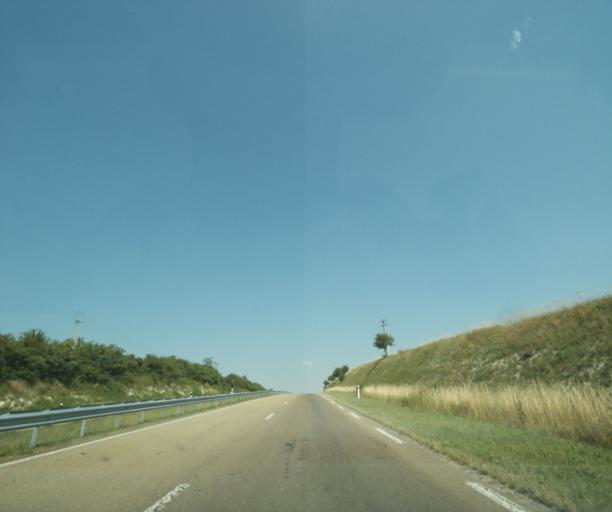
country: FR
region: Champagne-Ardenne
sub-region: Departement de la Marne
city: Fagnieres
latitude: 49.0521
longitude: 4.3028
